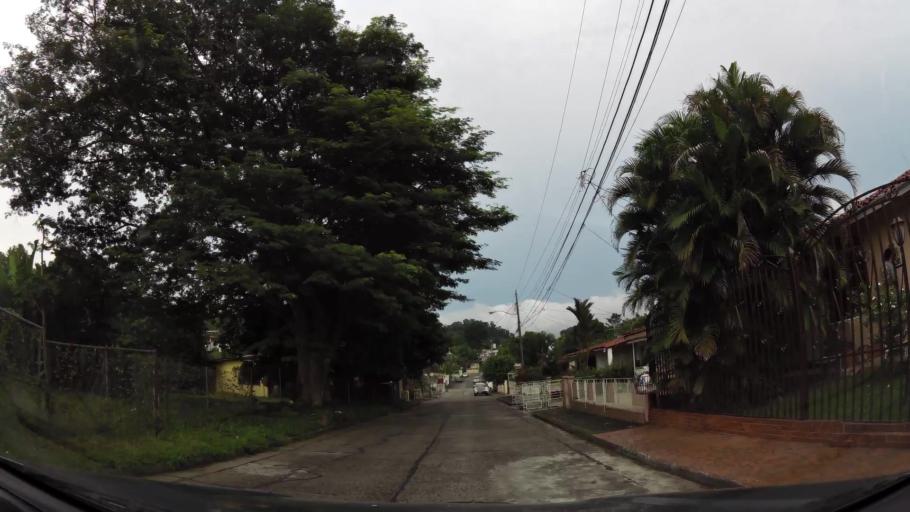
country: PA
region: Panama
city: Panama
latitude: 9.0081
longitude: -79.5276
